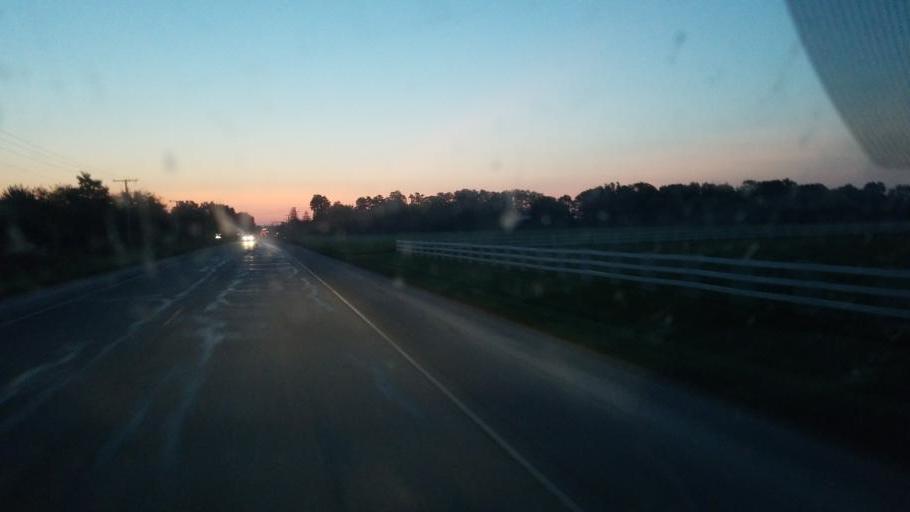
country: US
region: Indiana
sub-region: Elkhart County
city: Middlebury
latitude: 41.6761
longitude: -85.6042
